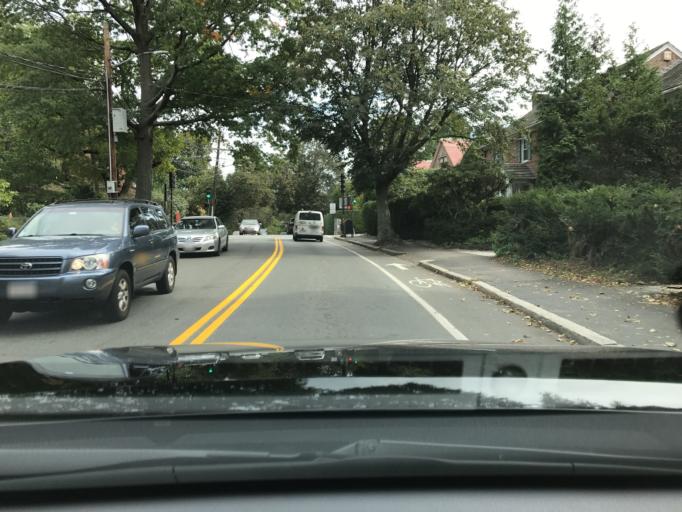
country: US
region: Massachusetts
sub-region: Norfolk County
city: Brookline
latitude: 42.3405
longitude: -71.1132
